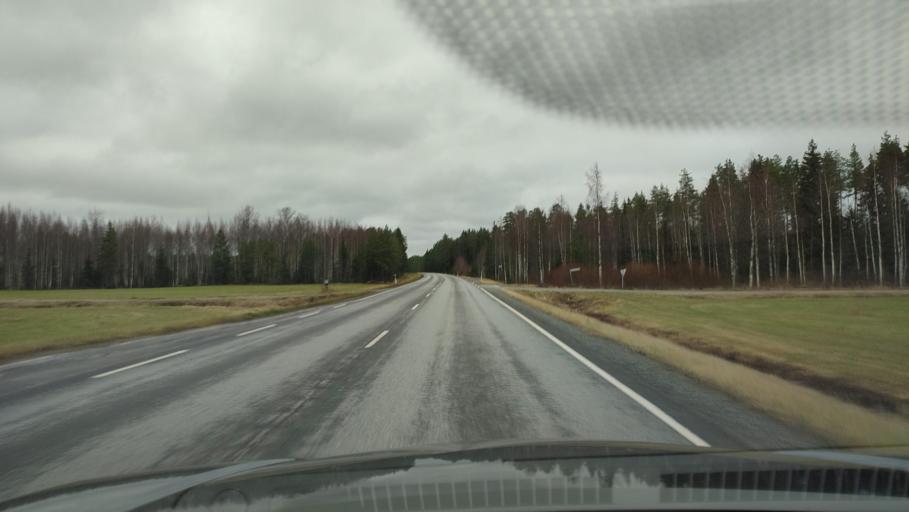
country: FI
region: Southern Ostrobothnia
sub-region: Suupohja
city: Kauhajoki
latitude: 62.4881
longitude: 22.2907
